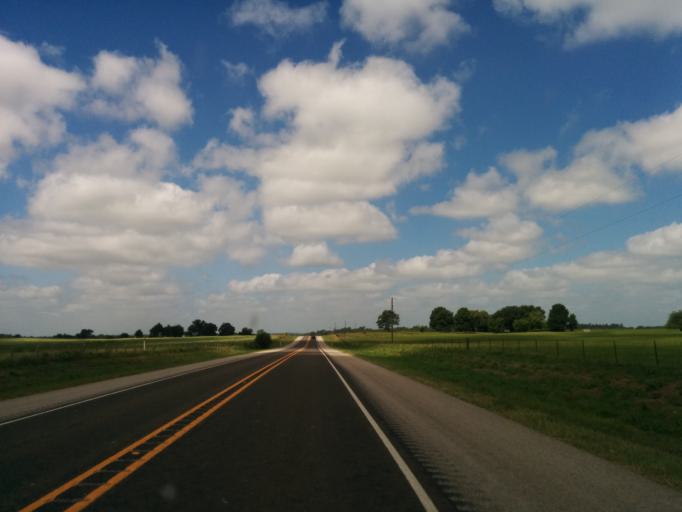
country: US
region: Texas
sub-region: Houston County
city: Crockett
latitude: 31.3193
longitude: -95.3875
